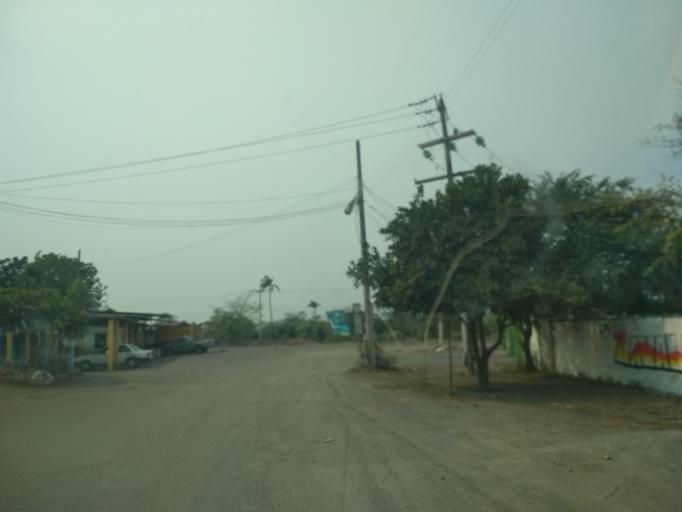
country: MX
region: Veracruz
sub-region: Veracruz
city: Delfino Victoria (Santa Fe)
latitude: 19.1932
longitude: -96.2863
